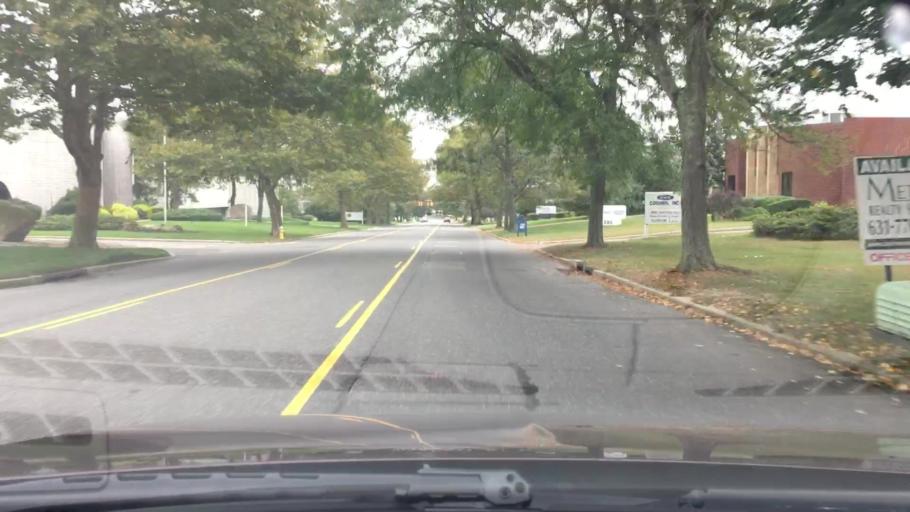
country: US
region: New York
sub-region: Suffolk County
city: Brentwood
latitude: 40.8166
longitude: -73.2593
